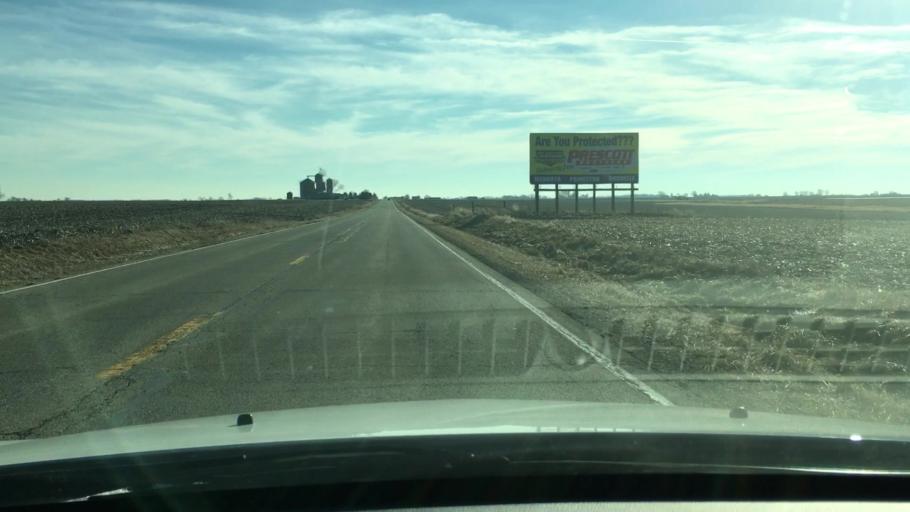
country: US
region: Illinois
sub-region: LaSalle County
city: Mendota
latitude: 41.5044
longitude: -89.1273
